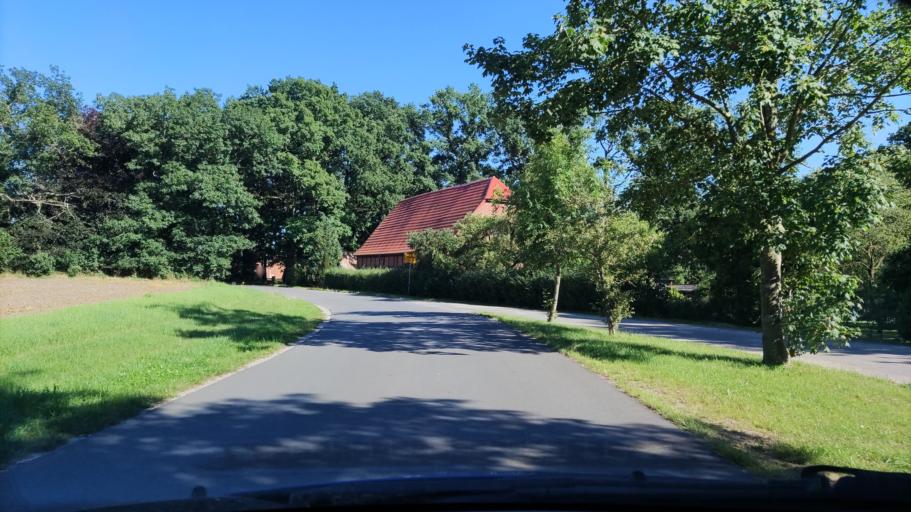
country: DE
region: Lower Saxony
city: Boitze
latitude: 53.1511
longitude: 10.7455
